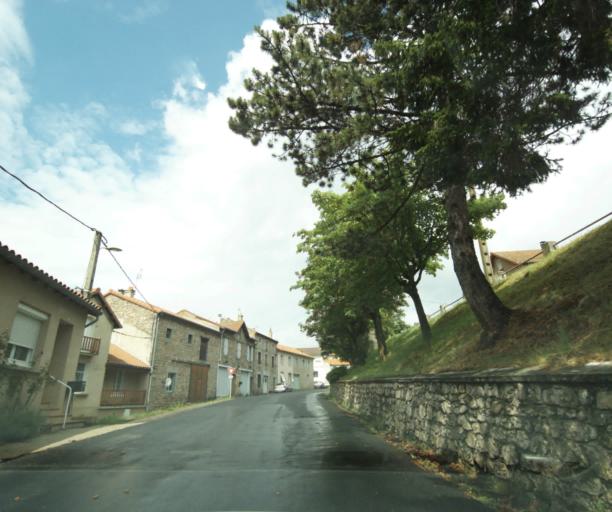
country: FR
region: Auvergne
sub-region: Departement de la Haute-Loire
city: Saugues
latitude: 44.9577
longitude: 3.5426
